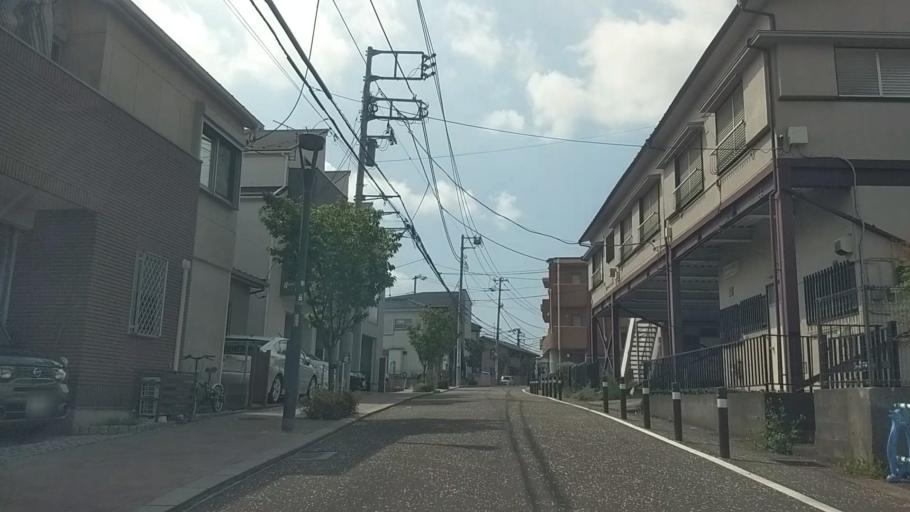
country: JP
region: Kanagawa
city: Yokohama
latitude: 35.3946
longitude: 139.5921
